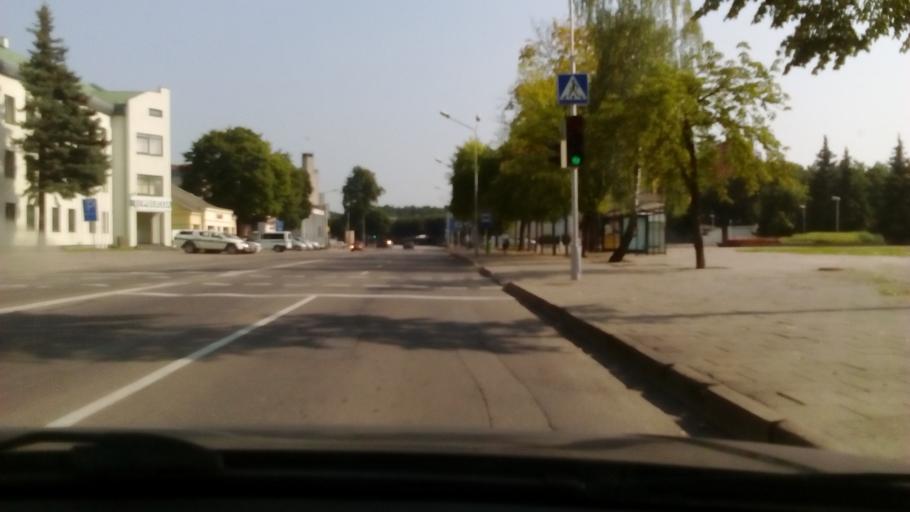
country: LT
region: Alytaus apskritis
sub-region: Alytus
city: Alytus
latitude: 54.3961
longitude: 24.0429
